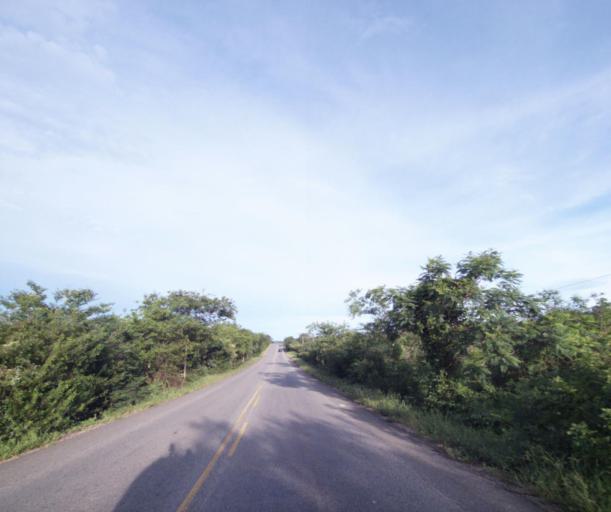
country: BR
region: Bahia
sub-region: Caetite
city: Caetite
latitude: -14.1675
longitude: -42.2485
